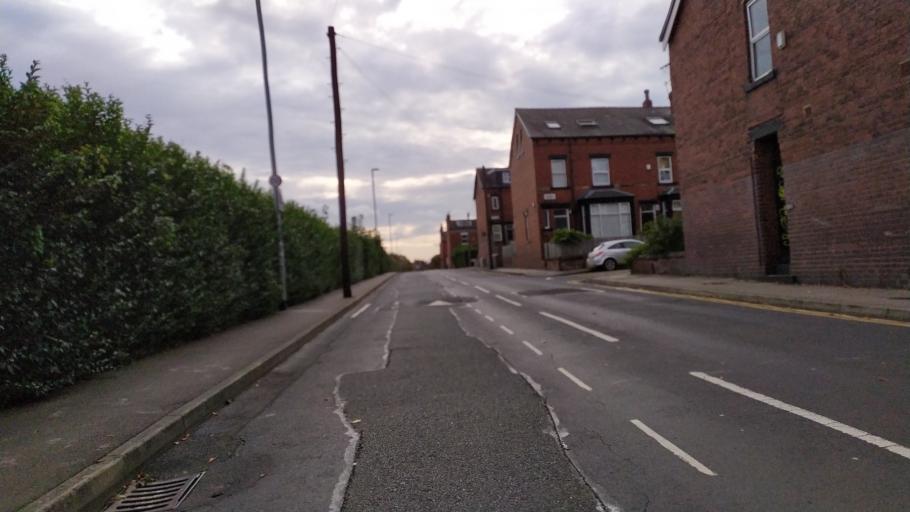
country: GB
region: England
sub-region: City and Borough of Leeds
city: Leeds
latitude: 53.8137
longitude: -1.5836
